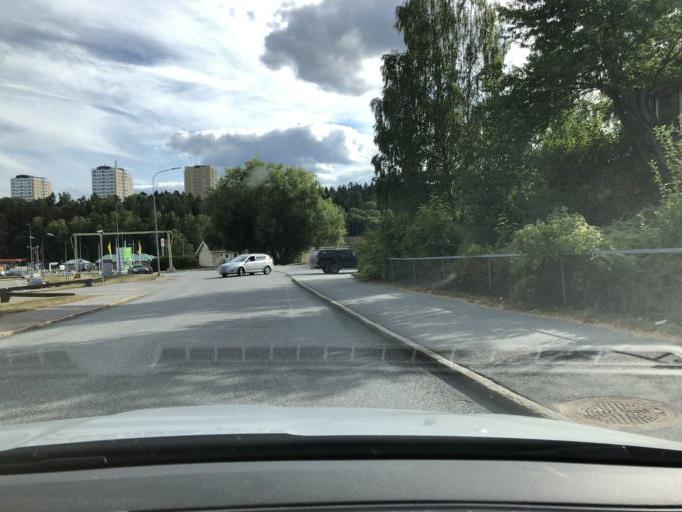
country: SE
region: Stockholm
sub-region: Sodertalje Kommun
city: Soedertaelje
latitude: 59.2044
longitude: 17.6083
